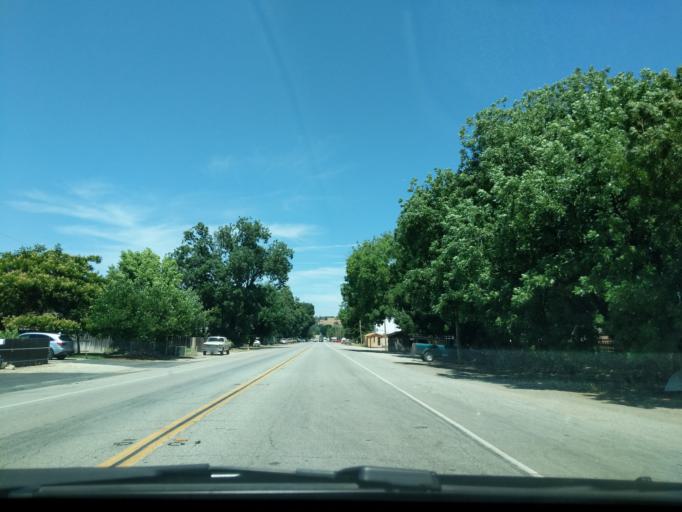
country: US
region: California
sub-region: San Luis Obispo County
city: Santa Margarita
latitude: 35.3870
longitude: -120.6163
